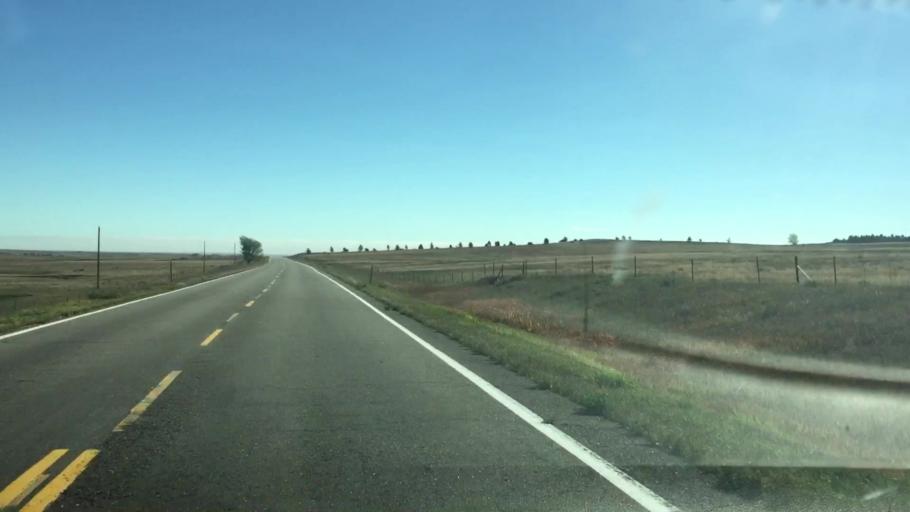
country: US
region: Colorado
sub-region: Lincoln County
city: Limon
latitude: 39.2880
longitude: -103.9550
